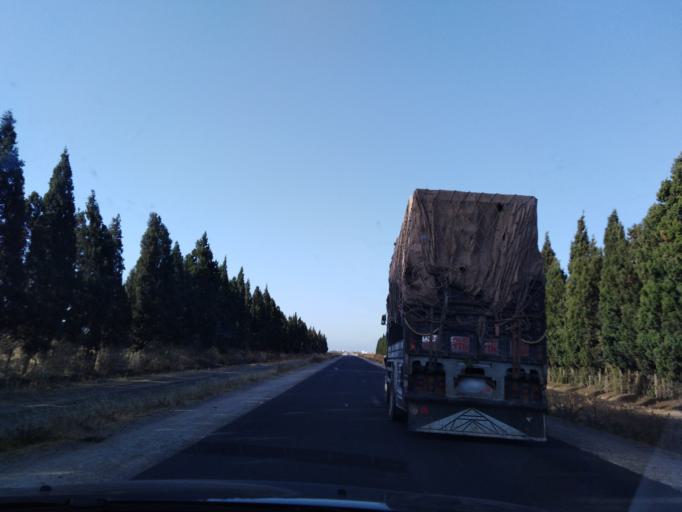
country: MA
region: Doukkala-Abda
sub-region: Safi
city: Safi
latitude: 32.5047
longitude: -8.9221
